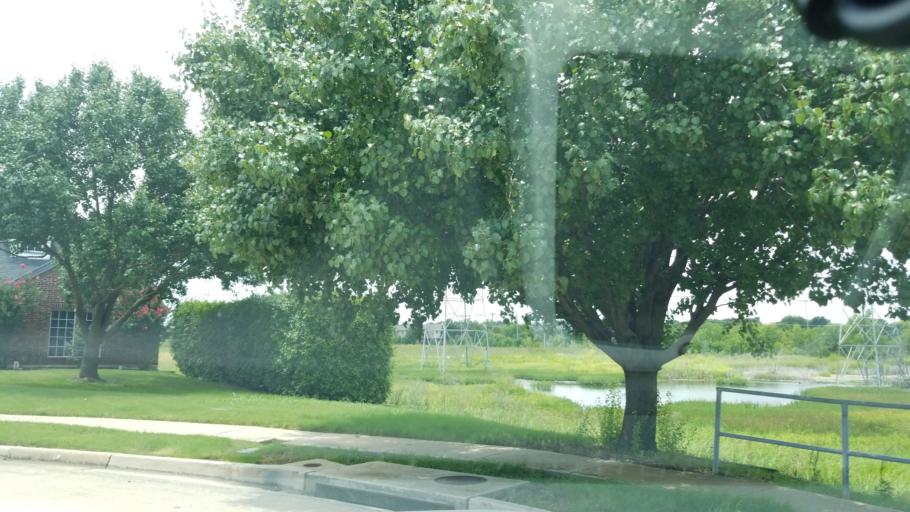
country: US
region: Texas
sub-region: Dallas County
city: Coppell
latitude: 32.9620
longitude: -96.9543
